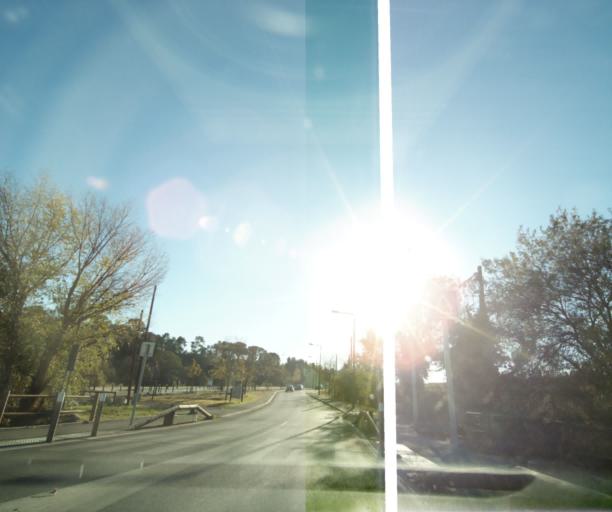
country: FR
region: Provence-Alpes-Cote d'Azur
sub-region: Departement des Bouches-du-Rhone
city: Plan-de-Cuques
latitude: 43.3406
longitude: 5.4422
